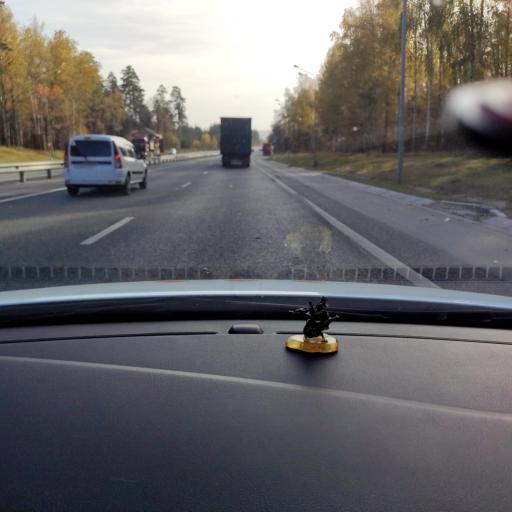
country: RU
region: Tatarstan
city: Osinovo
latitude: 55.8316
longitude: 48.8494
